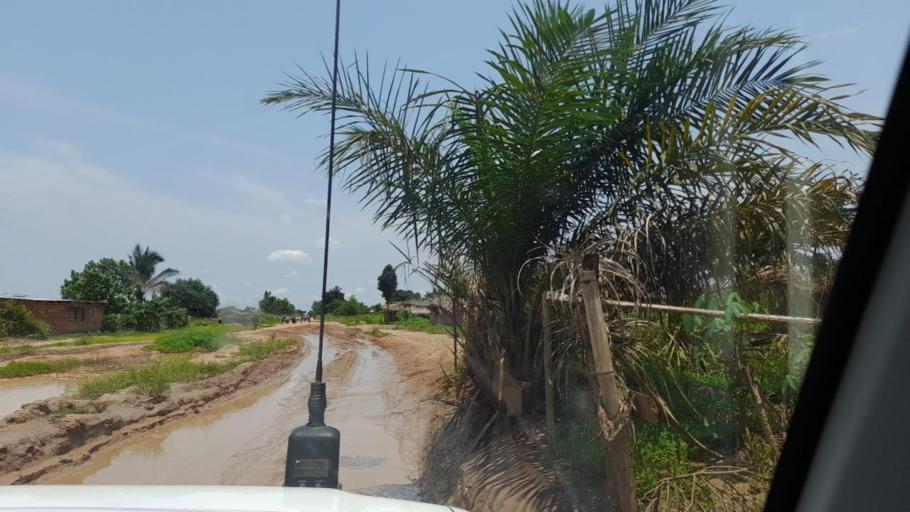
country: CD
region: Kasai-Occidental
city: Kananga
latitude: -5.9464
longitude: 22.2785
